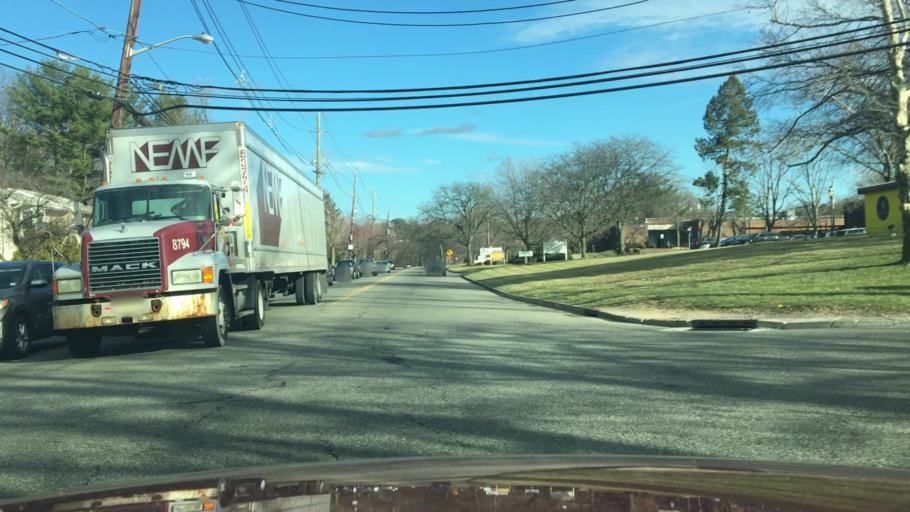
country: US
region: New Jersey
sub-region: Middlesex County
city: Milltown
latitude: 40.4542
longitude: -74.4184
